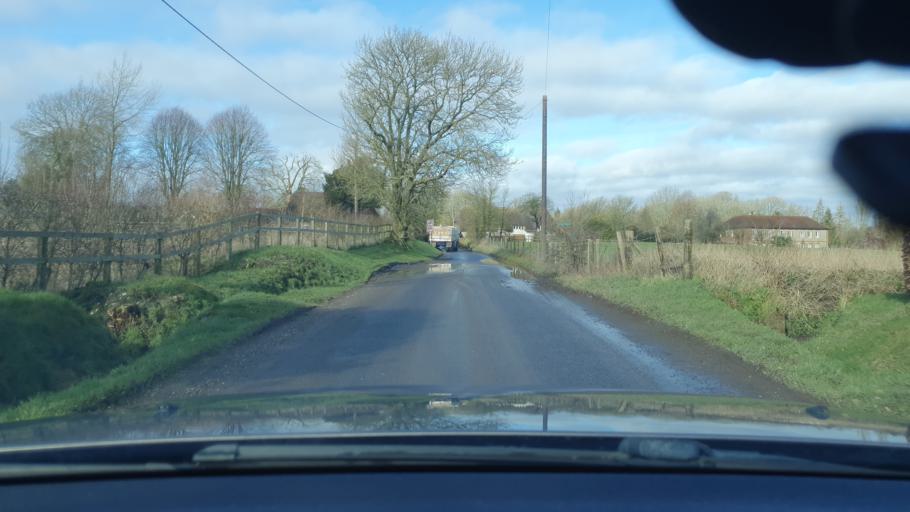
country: GB
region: England
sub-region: Wiltshire
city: Shalbourne
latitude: 51.3611
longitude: -1.5257
